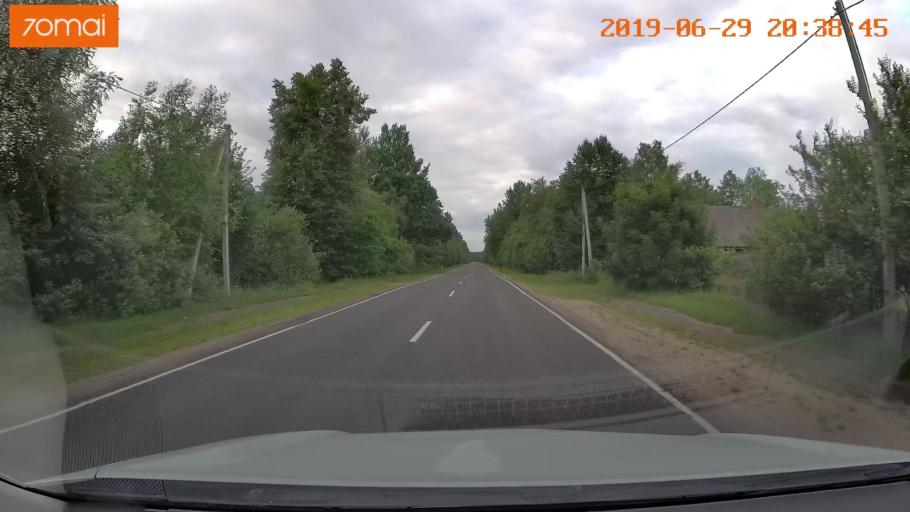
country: BY
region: Brest
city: Hantsavichy
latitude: 52.5538
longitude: 26.3641
